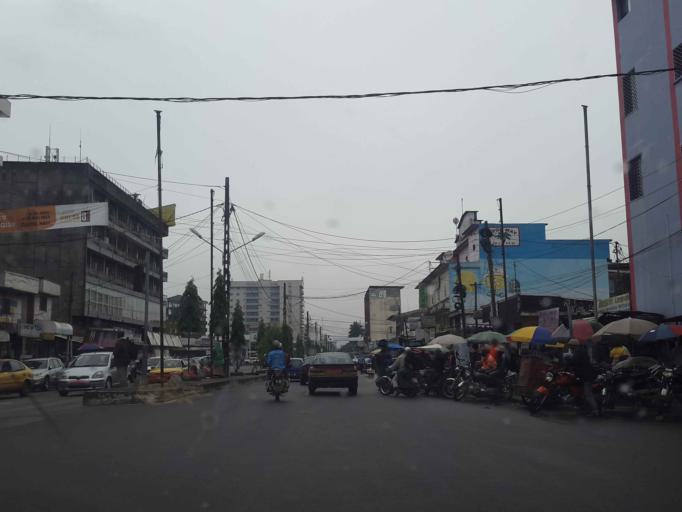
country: CM
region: Littoral
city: Douala
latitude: 4.0459
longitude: 9.6987
